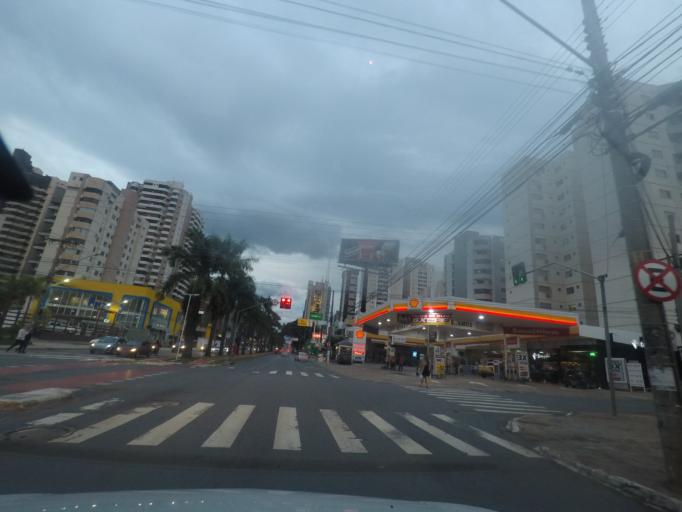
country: BR
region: Goias
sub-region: Goiania
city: Goiania
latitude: -16.7142
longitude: -49.2693
